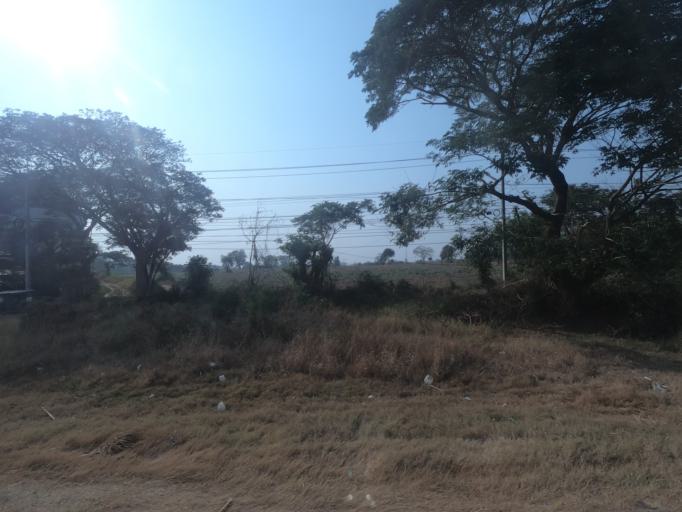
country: TH
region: Khon Kaen
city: Ban Haet
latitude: 16.2936
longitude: 102.7868
